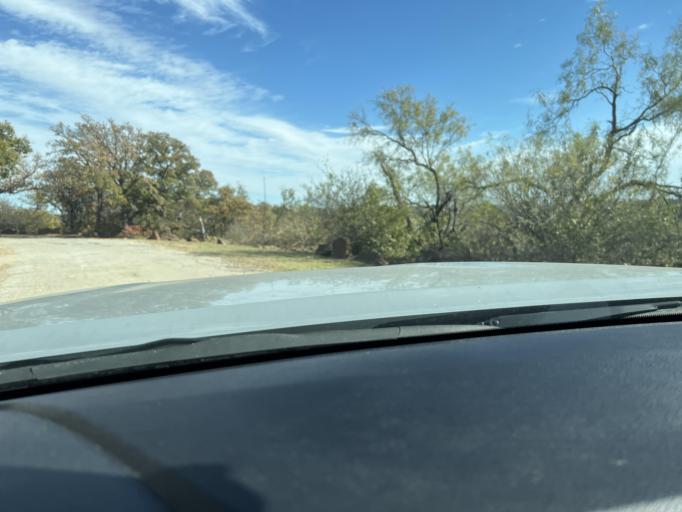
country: US
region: Texas
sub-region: Eastland County
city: Eastland
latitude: 32.3970
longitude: -98.8331
